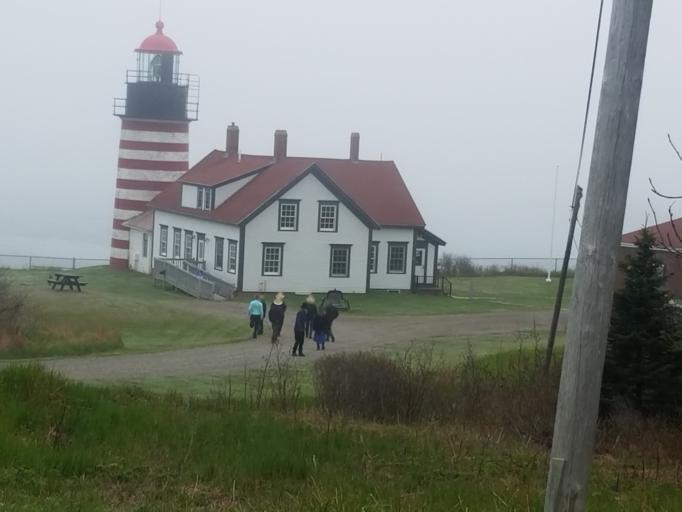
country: US
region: Maine
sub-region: Washington County
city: Eastport
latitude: 44.8156
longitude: -66.9518
